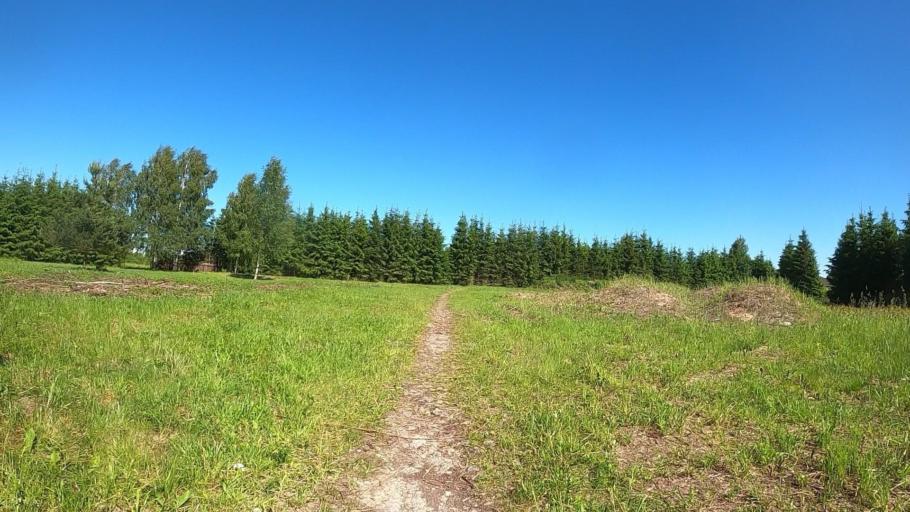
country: LV
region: Salaspils
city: Salaspils
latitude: 56.8434
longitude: 24.3952
